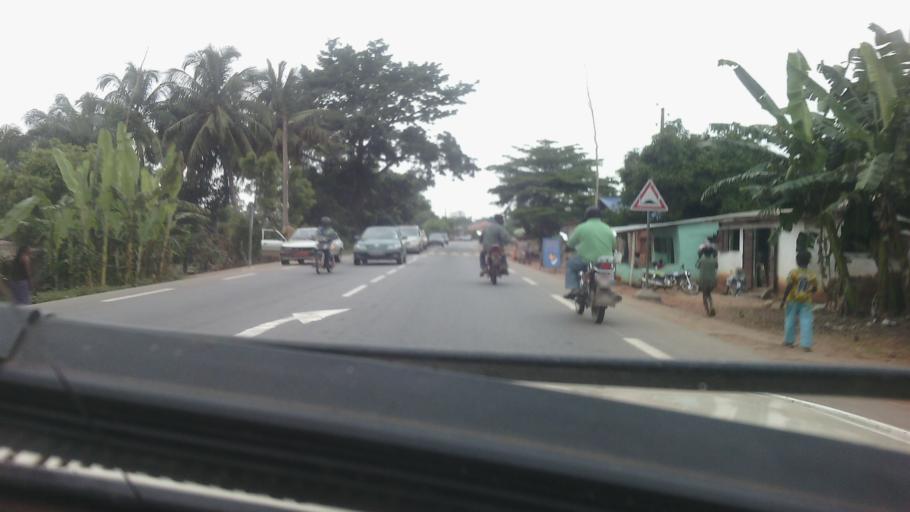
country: BJ
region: Mono
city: Come
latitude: 6.3910
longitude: 1.9477
